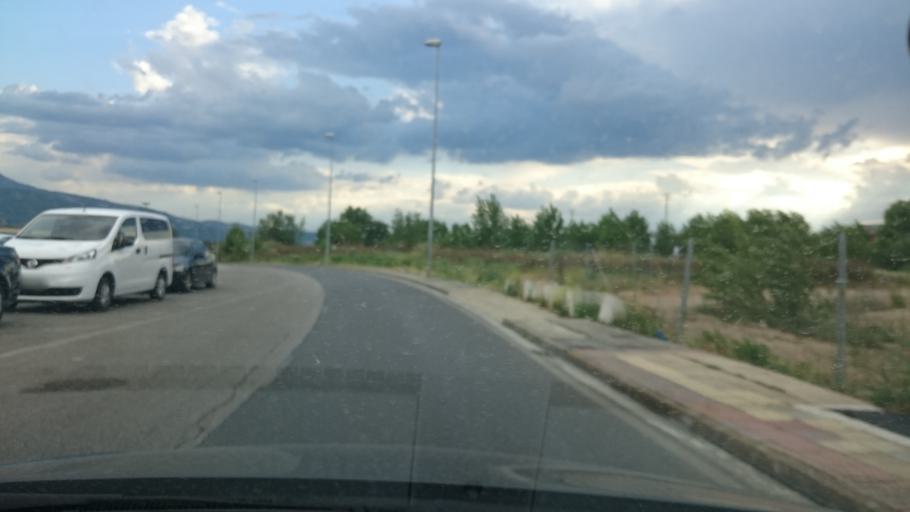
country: ES
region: Castille and Leon
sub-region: Provincia de Leon
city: Ponferrada
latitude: 42.5554
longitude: -6.6175
